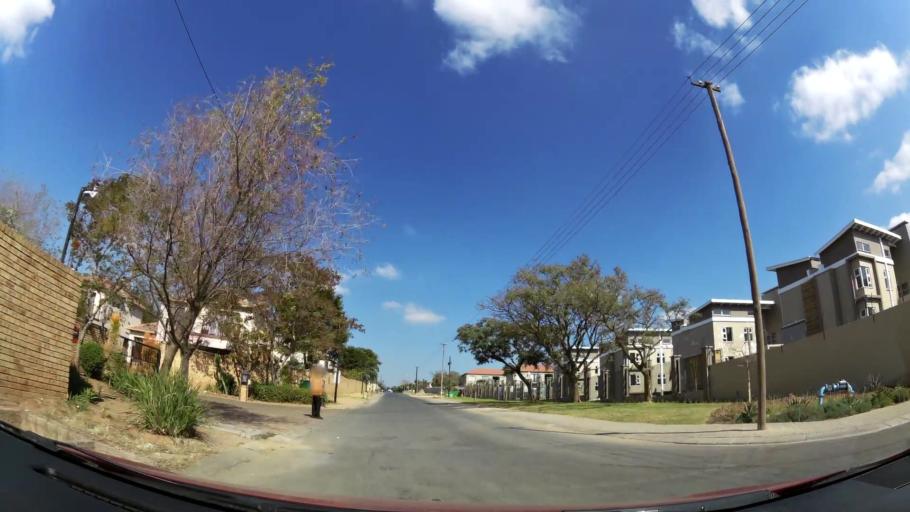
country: ZA
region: Gauteng
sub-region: West Rand District Municipality
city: Muldersdriseloop
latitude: -26.0524
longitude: 27.9516
